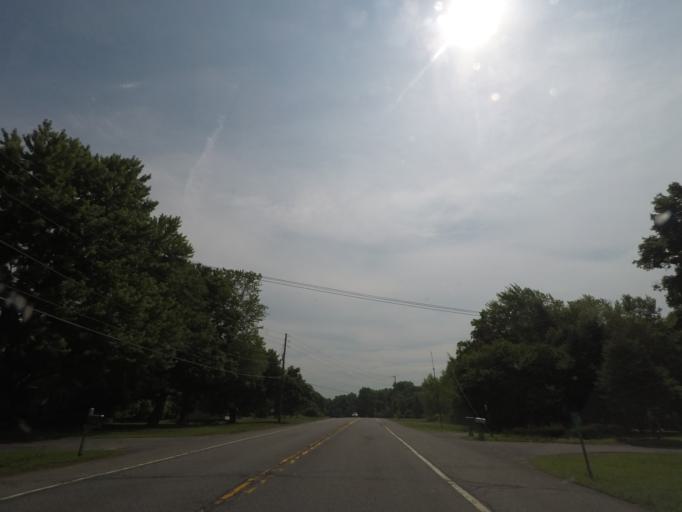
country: US
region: New York
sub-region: Saratoga County
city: Mechanicville
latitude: 42.8852
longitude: -73.6998
